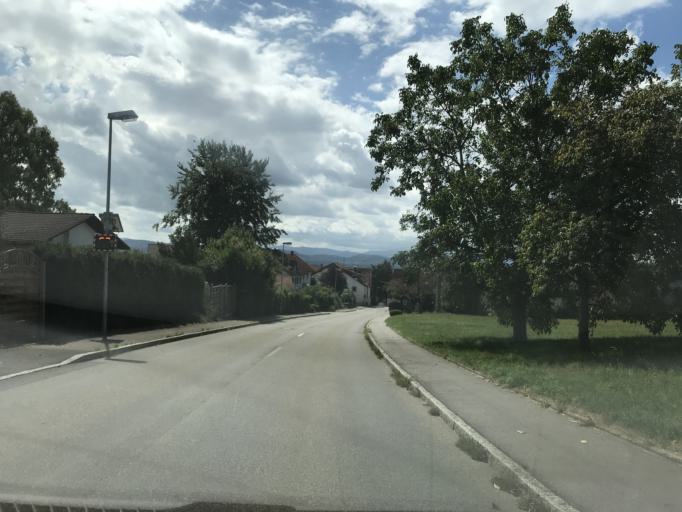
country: DE
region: Baden-Wuerttemberg
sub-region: Freiburg Region
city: Steinen
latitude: 47.6021
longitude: 7.7600
